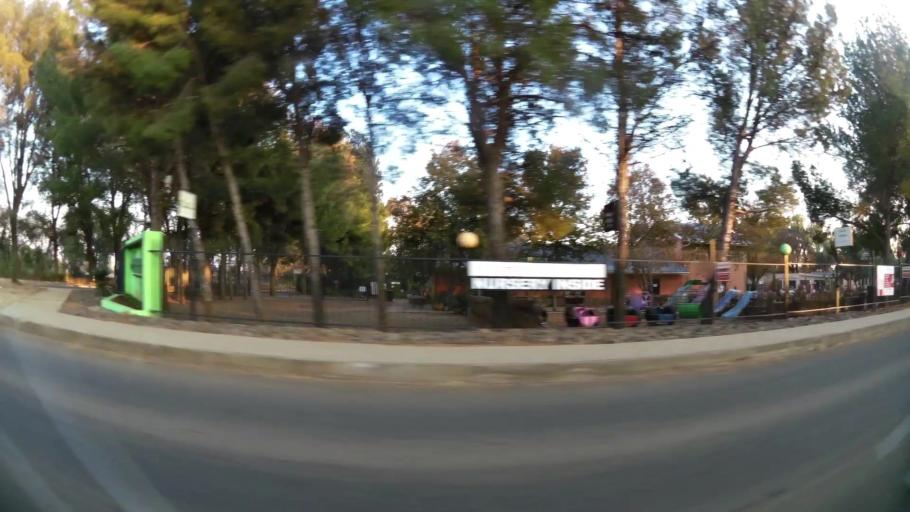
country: ZA
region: Orange Free State
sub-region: Mangaung Metropolitan Municipality
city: Bloemfontein
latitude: -29.0885
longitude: 26.1532
